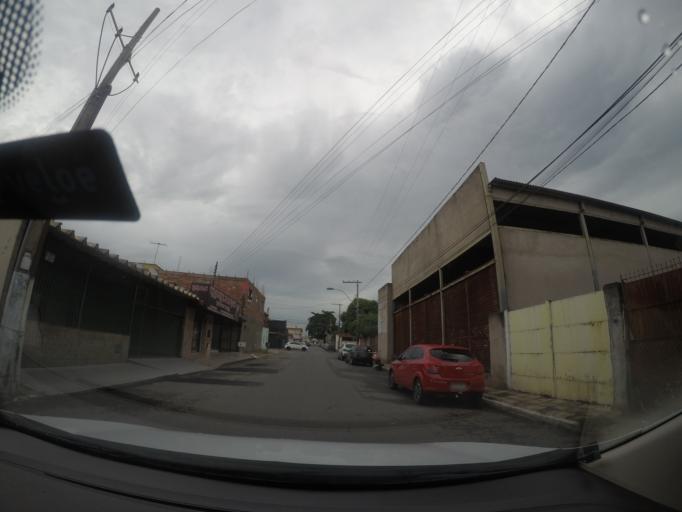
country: BR
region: Goias
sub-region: Goiania
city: Goiania
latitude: -16.6665
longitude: -49.2889
